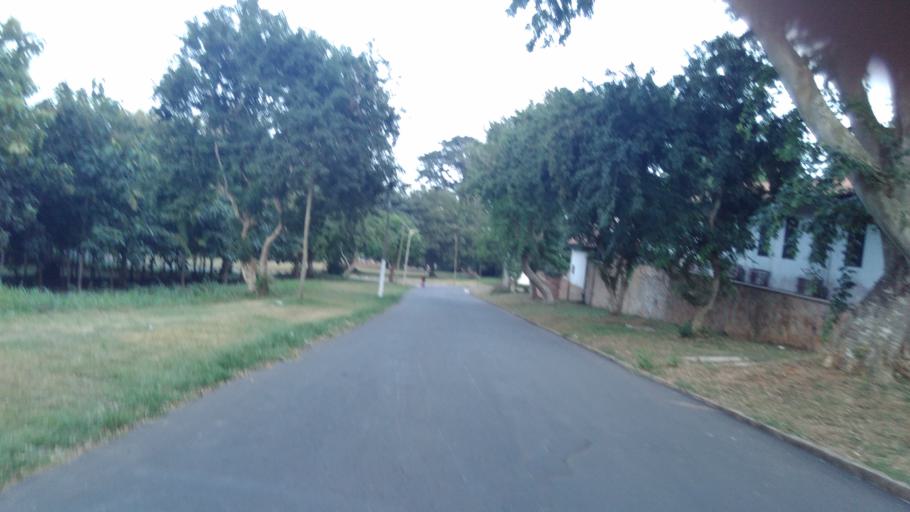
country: GH
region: Greater Accra
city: Medina Estates
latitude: 5.6511
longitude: -0.1948
